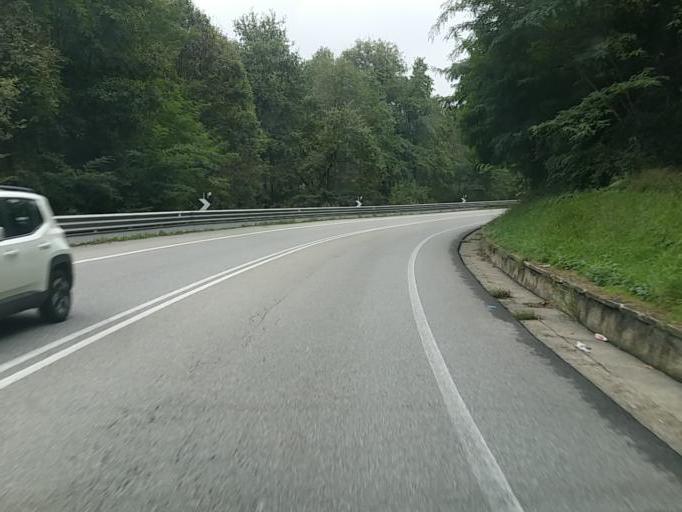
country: IT
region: Lombardy
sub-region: Provincia di Varese
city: Buguggiate
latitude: 45.7911
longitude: 8.8101
